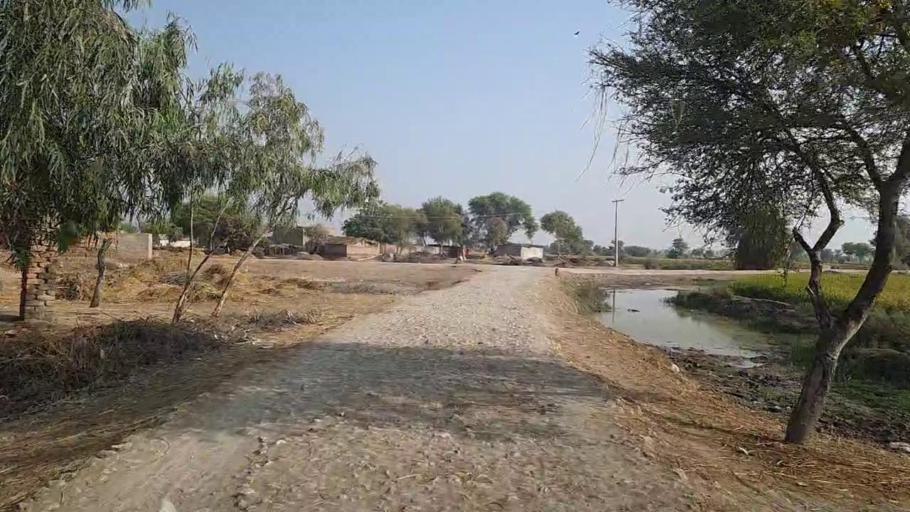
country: PK
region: Sindh
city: Kandhkot
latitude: 28.2875
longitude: 69.2577
